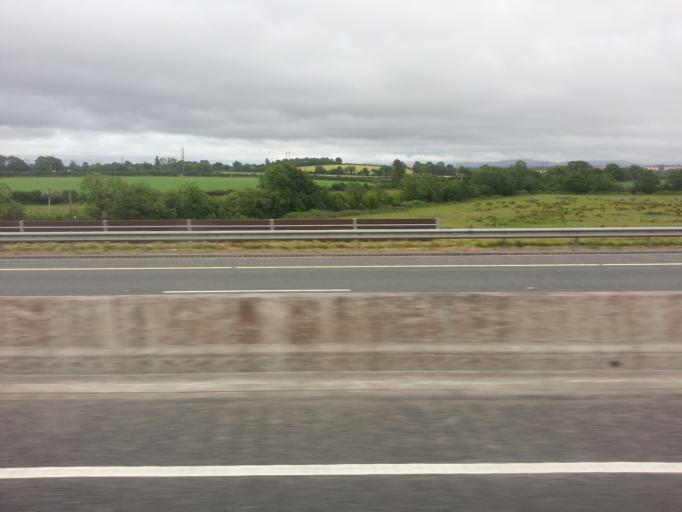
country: IE
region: Leinster
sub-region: County Carlow
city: Carlow
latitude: 52.8304
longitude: -6.8489
